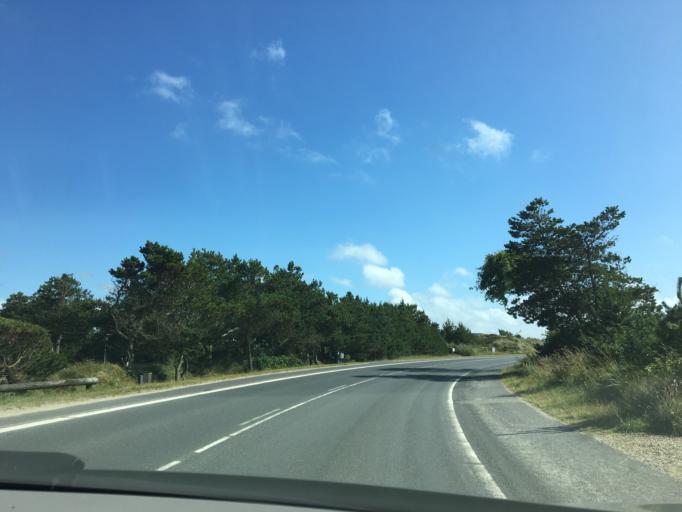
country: DK
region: South Denmark
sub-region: Varde Kommune
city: Oksbol
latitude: 55.7372
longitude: 8.1847
